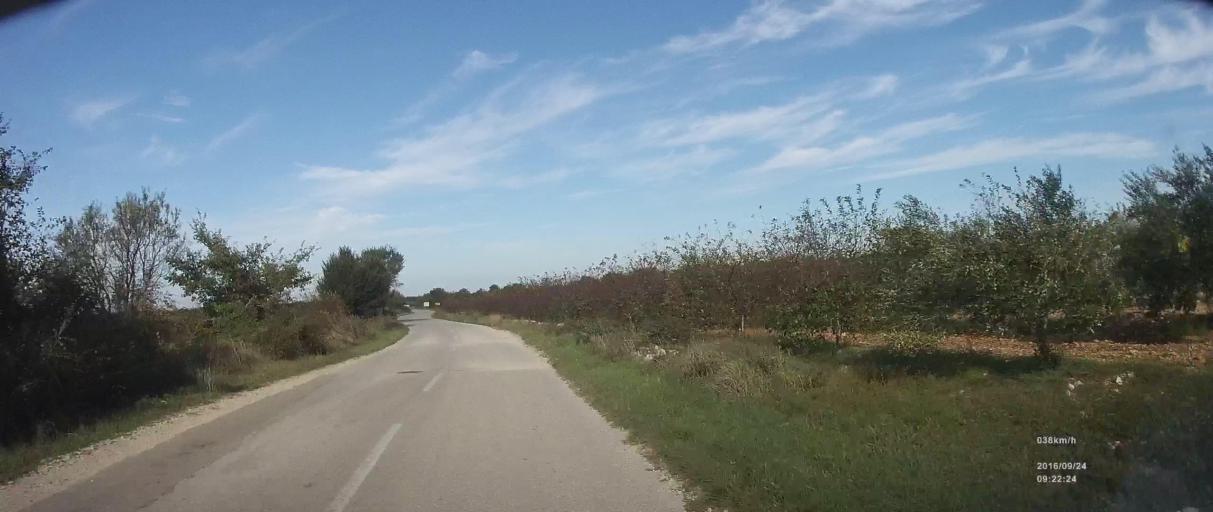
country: HR
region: Zadarska
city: Polaca
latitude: 44.0696
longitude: 15.4808
